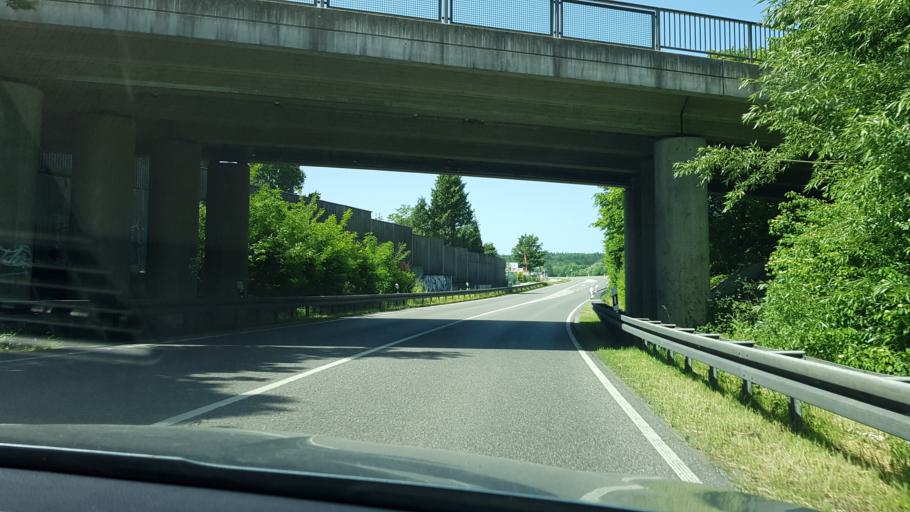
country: DE
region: Bavaria
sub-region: Upper Bavaria
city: Schongeising
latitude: 48.1424
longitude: 11.2003
